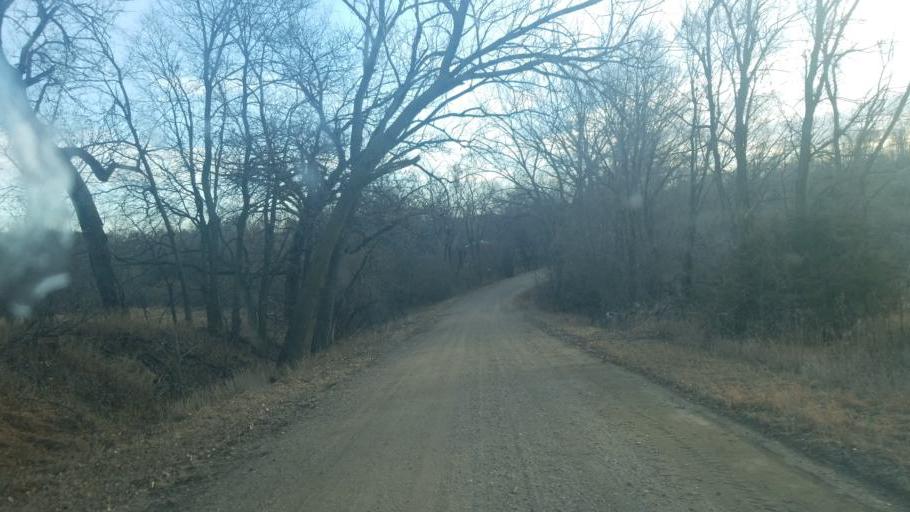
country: US
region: Nebraska
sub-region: Knox County
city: Center
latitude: 42.6996
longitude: -97.8374
